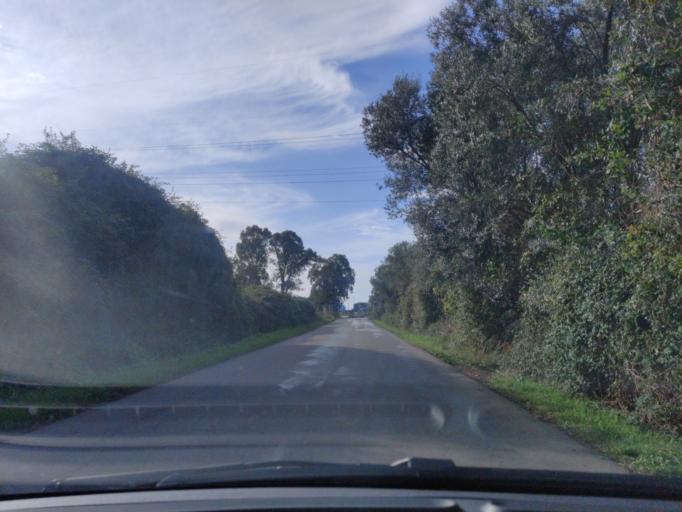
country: IT
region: Latium
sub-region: Citta metropolitana di Roma Capitale
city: Aurelia
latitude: 42.1325
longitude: 11.7879
